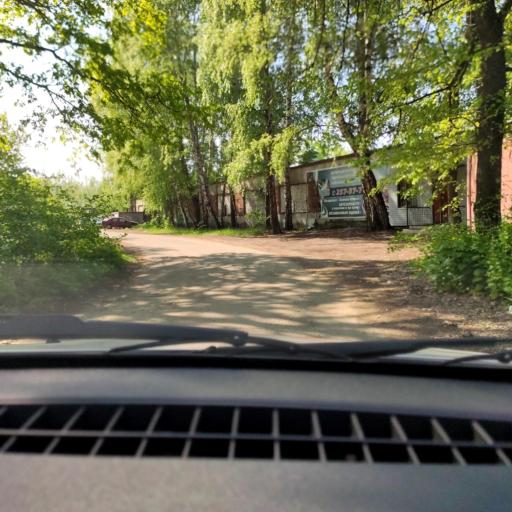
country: RU
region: Voronezj
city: Podgornoye
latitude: 51.7437
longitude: 39.1726
